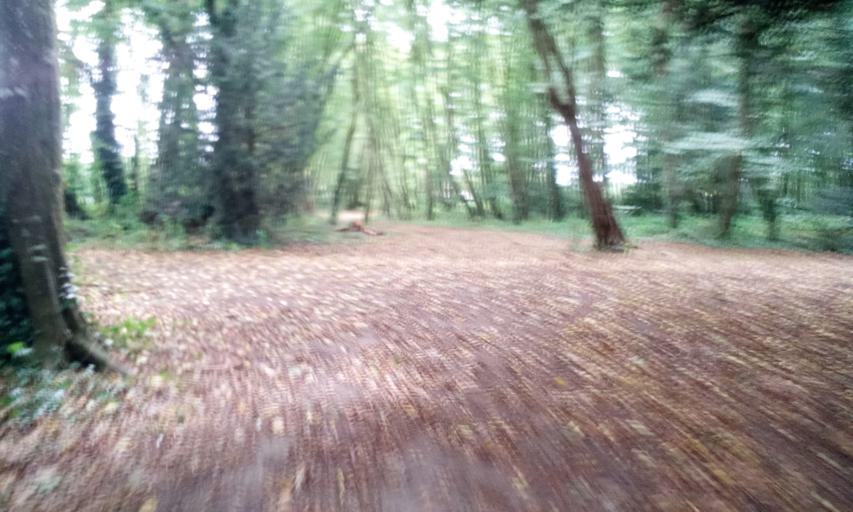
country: FR
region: Lower Normandy
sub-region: Departement du Calvados
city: Mouen
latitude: 49.1343
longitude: -0.4799
